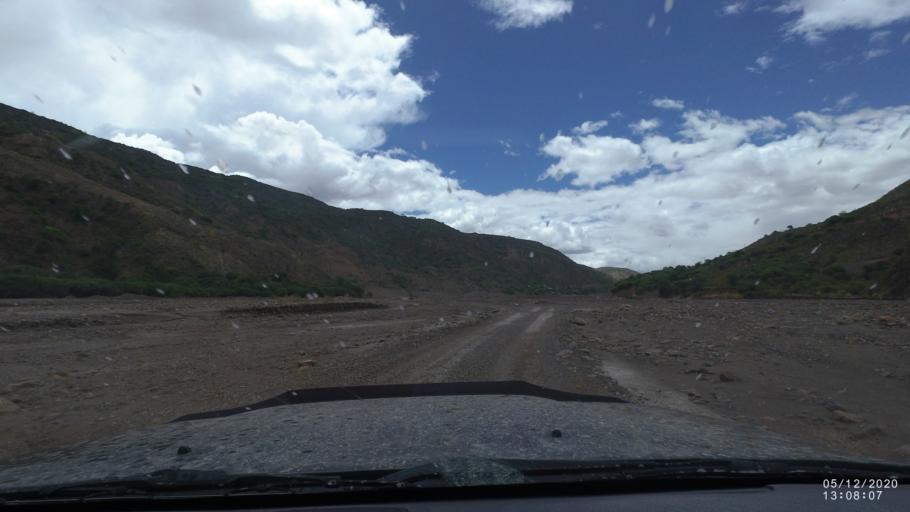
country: BO
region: Cochabamba
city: Sipe Sipe
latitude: -17.5613
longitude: -66.4508
